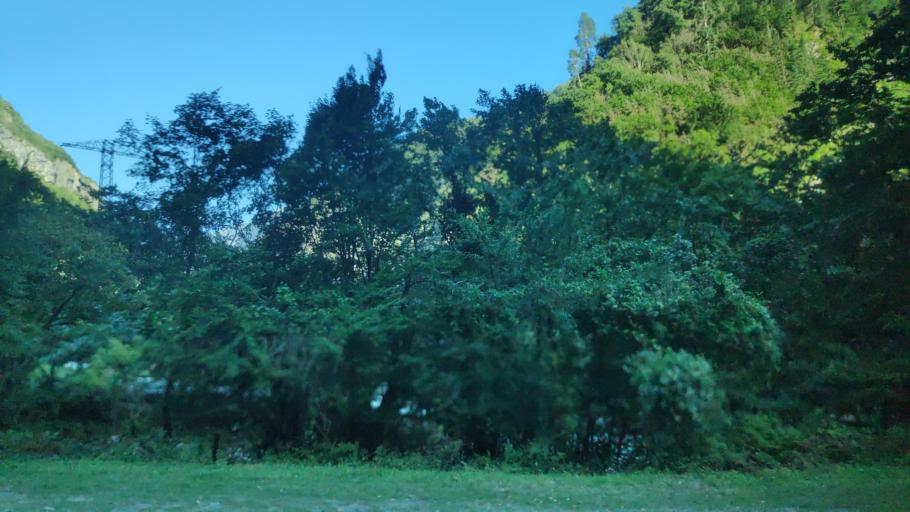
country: GE
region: Abkhazia
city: Gagra
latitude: 43.3688
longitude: 40.4577
